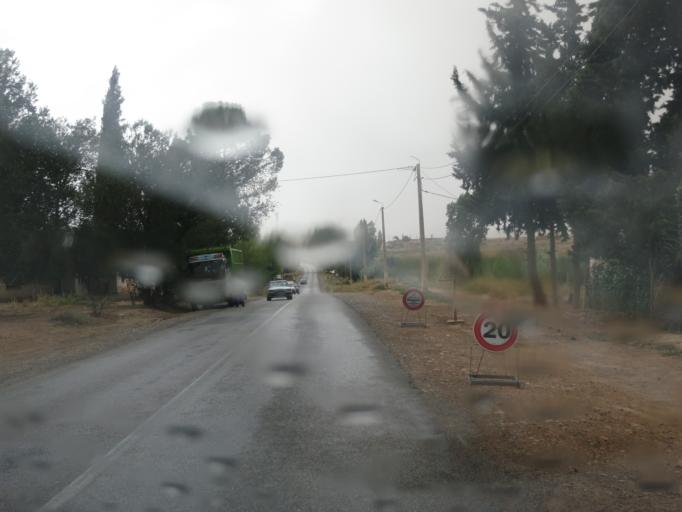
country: MA
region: Meknes-Tafilalet
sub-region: Khenifra
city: Itzer
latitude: 32.8792
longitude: -4.9493
